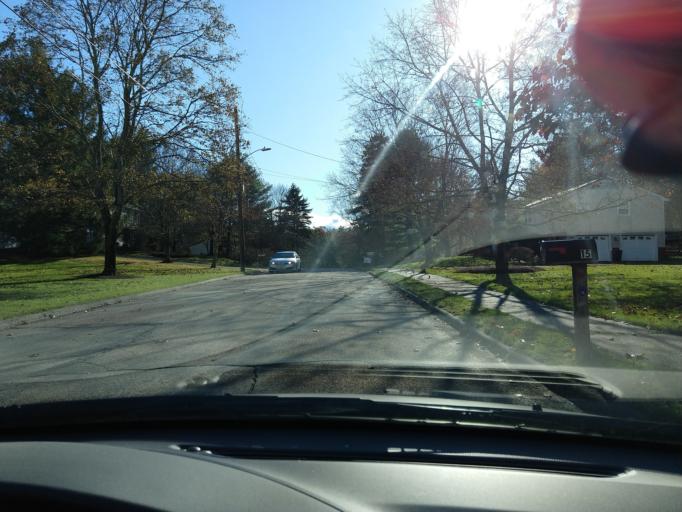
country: US
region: Massachusetts
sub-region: Middlesex County
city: Pinehurst
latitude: 42.4989
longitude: -71.2424
